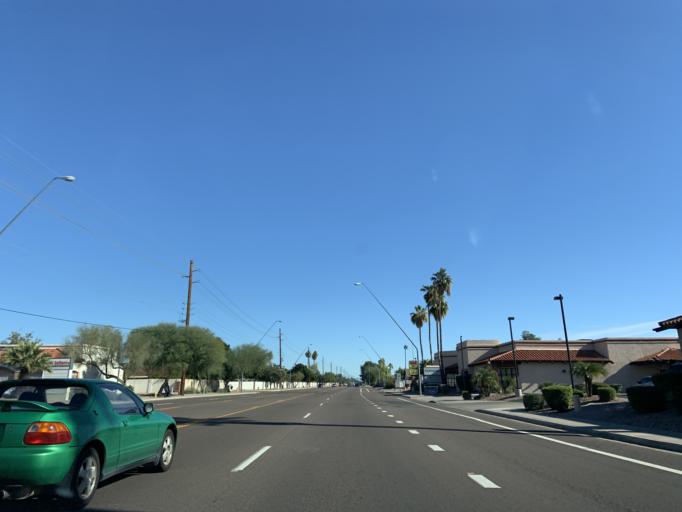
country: US
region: Arizona
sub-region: Maricopa County
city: San Carlos
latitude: 33.3642
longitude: -111.8578
